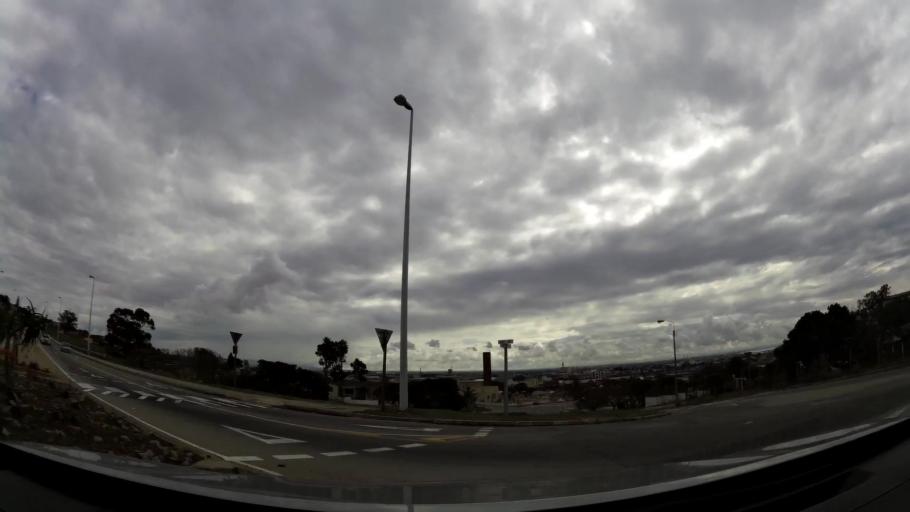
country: ZA
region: Eastern Cape
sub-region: Nelson Mandela Bay Metropolitan Municipality
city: Port Elizabeth
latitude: -33.9434
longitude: 25.5907
